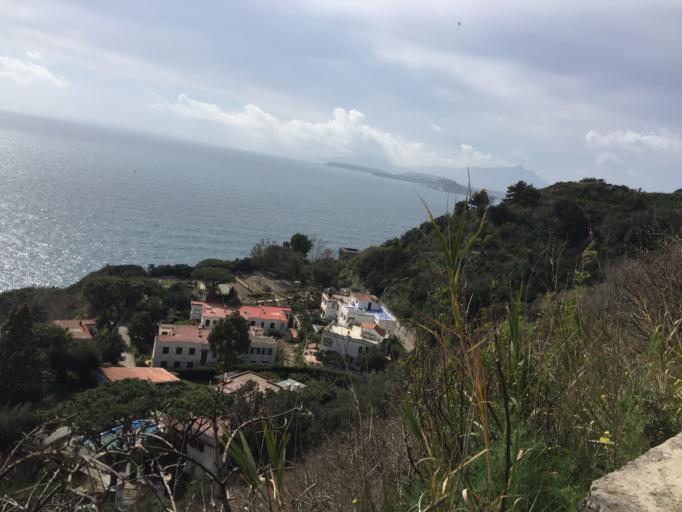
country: IT
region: Campania
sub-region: Provincia di Napoli
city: Bacoli
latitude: 40.7809
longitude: 14.0889
